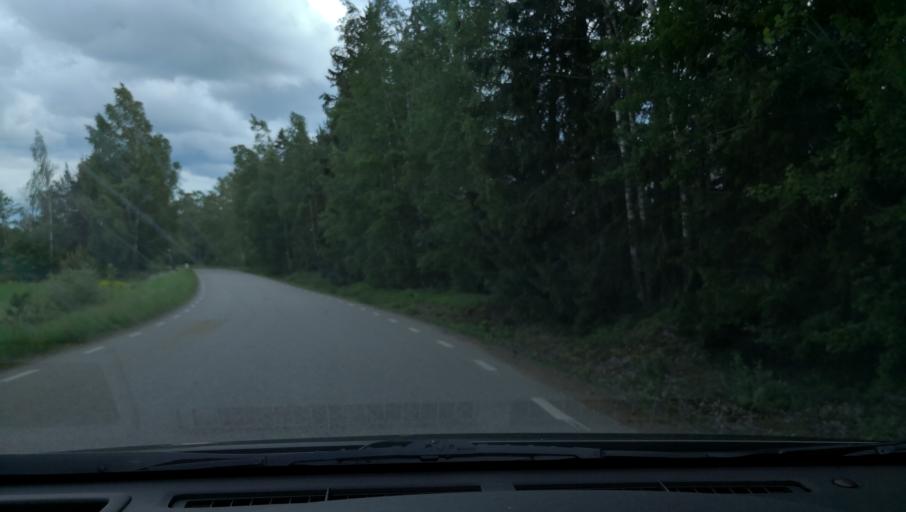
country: SE
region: OErebro
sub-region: Lindesbergs Kommun
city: Fellingsbro
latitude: 59.3312
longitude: 15.6677
